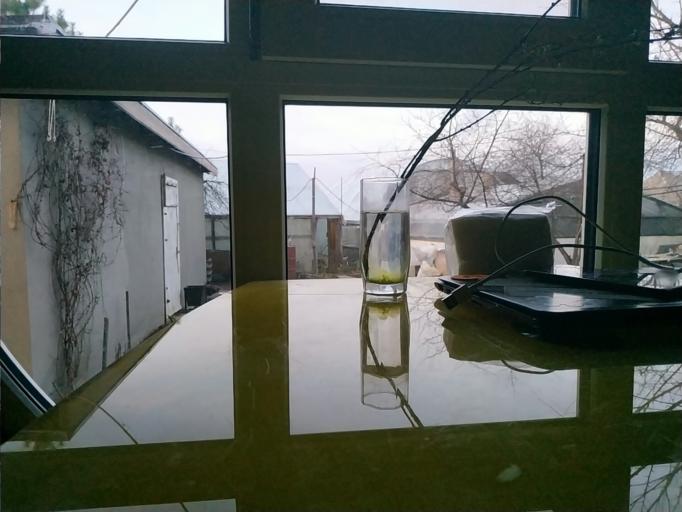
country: RU
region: Republic of Karelia
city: Sukkozero
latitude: 62.6554
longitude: 31.9101
